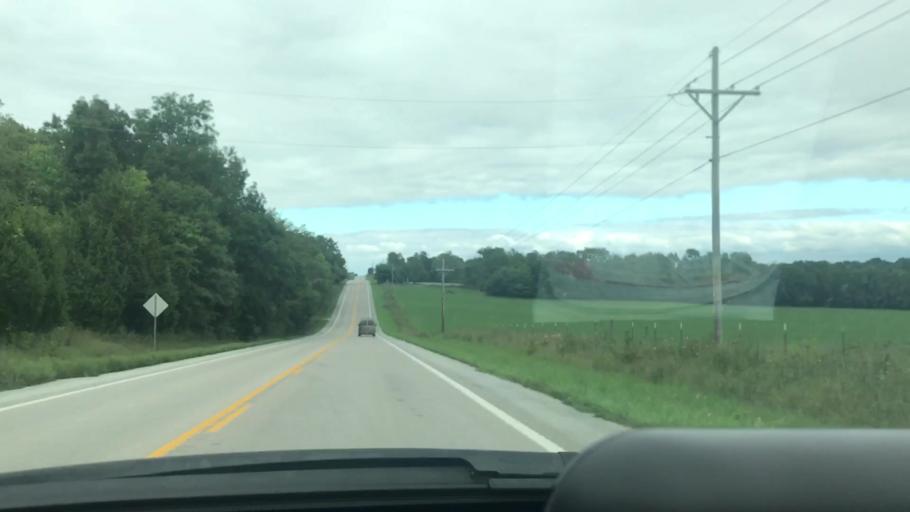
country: US
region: Missouri
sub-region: Hickory County
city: Hermitage
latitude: 37.8756
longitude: -93.1805
